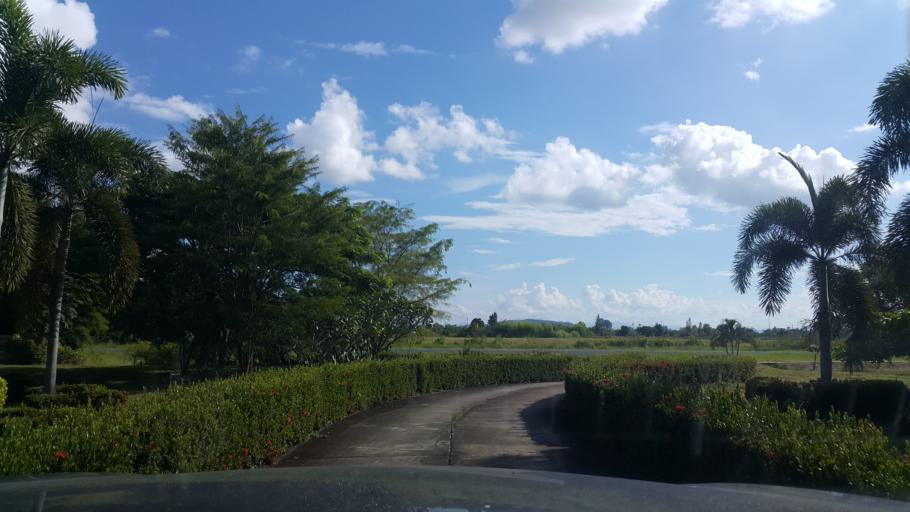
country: TH
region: Lamphun
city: Ban Thi
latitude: 18.6771
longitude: 99.1056
